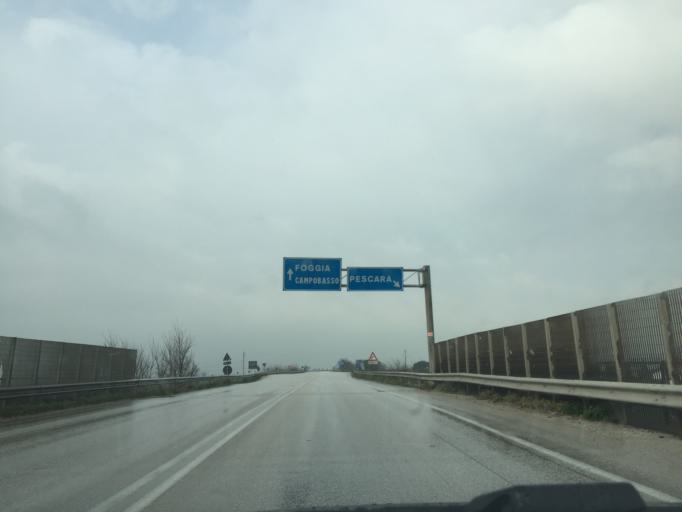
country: IT
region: Apulia
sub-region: Provincia di Foggia
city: Foggia
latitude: 41.4979
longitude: 15.5232
